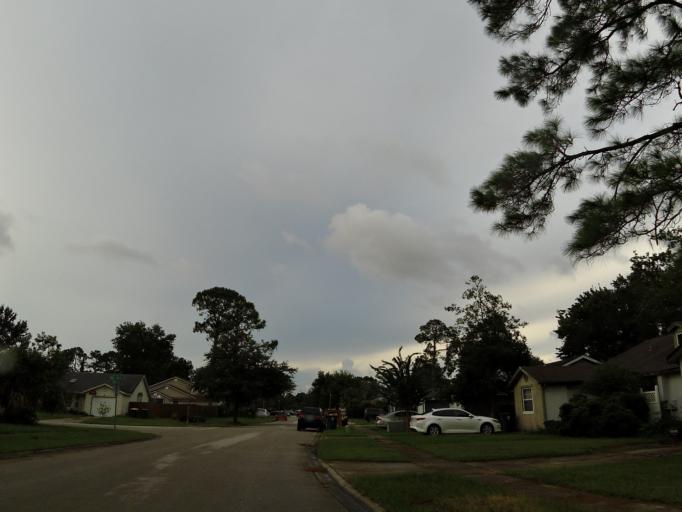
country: US
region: Florida
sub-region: Duval County
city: Neptune Beach
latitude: 30.3018
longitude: -81.5147
